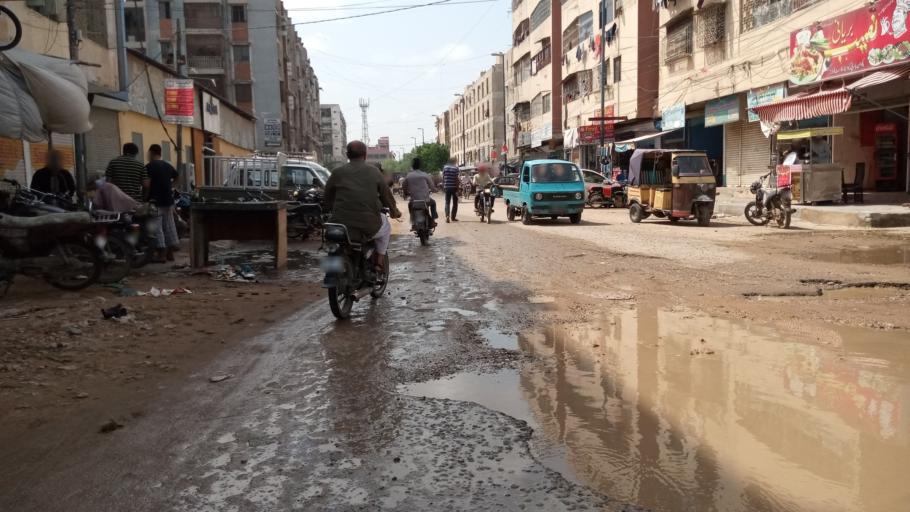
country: PK
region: Sindh
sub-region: Karachi District
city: Karachi
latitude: 24.9272
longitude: 67.0680
